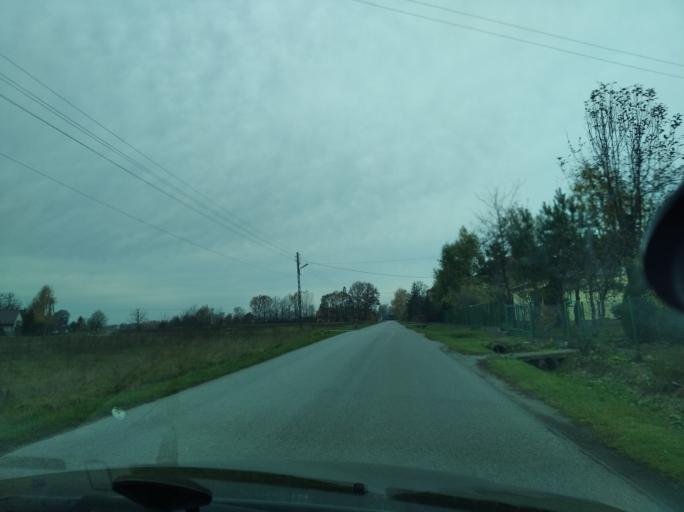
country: PL
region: Subcarpathian Voivodeship
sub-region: Powiat przeworski
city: Grzeska
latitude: 50.0927
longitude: 22.4431
